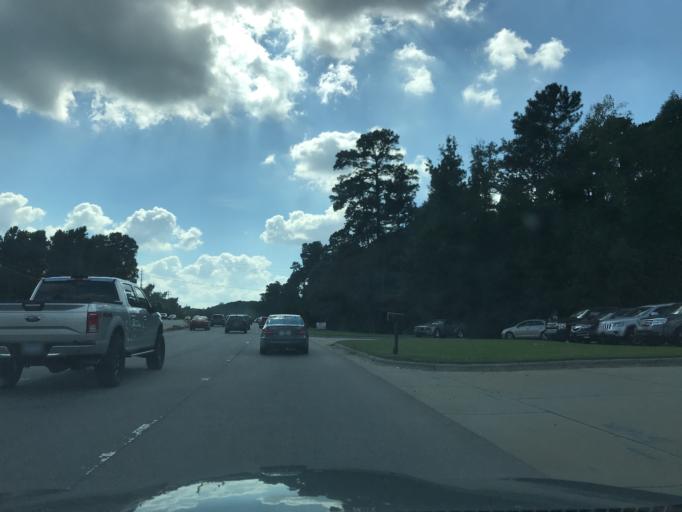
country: US
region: North Carolina
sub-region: Wake County
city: Rolesville
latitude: 35.8757
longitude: -78.5408
